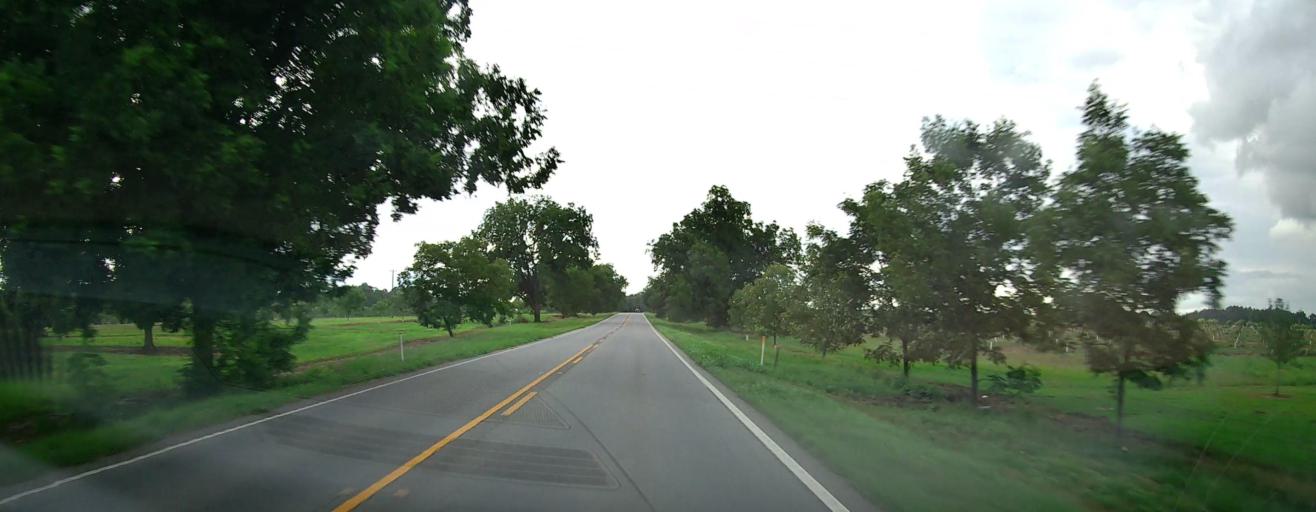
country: US
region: Georgia
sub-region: Houston County
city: Perry
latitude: 32.4450
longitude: -83.6622
